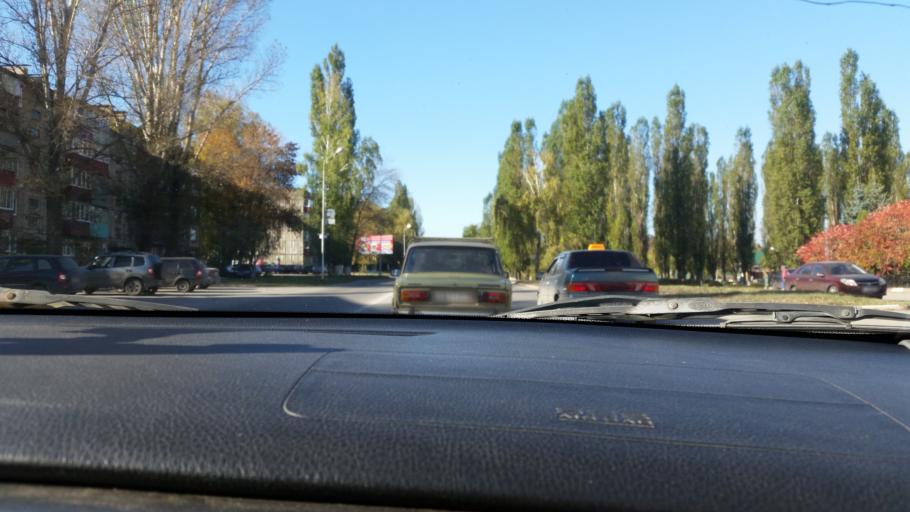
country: RU
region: Lipetsk
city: Gryazi
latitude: 52.4917
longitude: 39.9612
